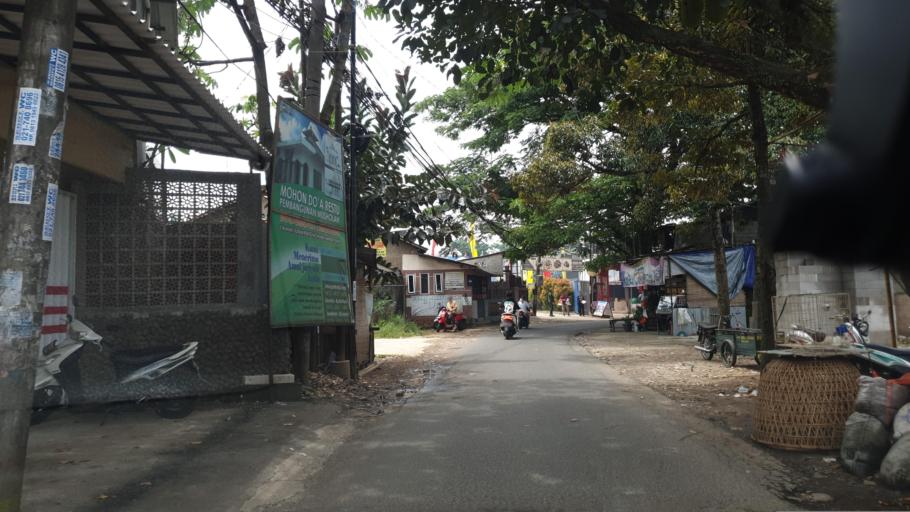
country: ID
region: West Java
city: Pamulang
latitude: -6.3681
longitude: 106.7621
